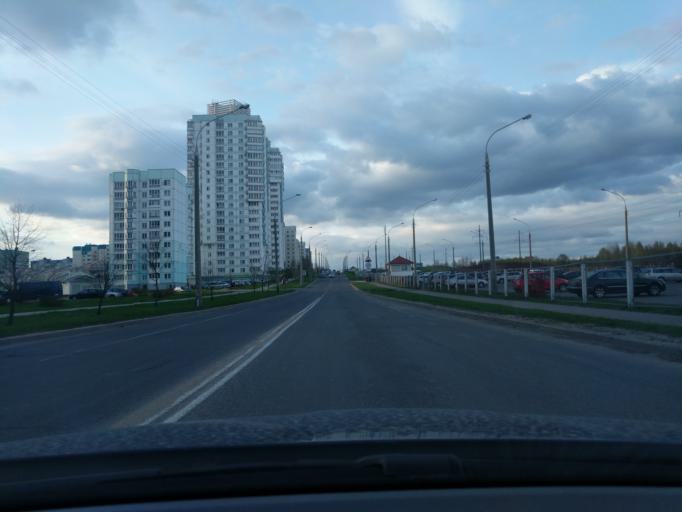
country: BY
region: Minsk
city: Novoye Medvezhino
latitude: 53.8939
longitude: 27.4628
